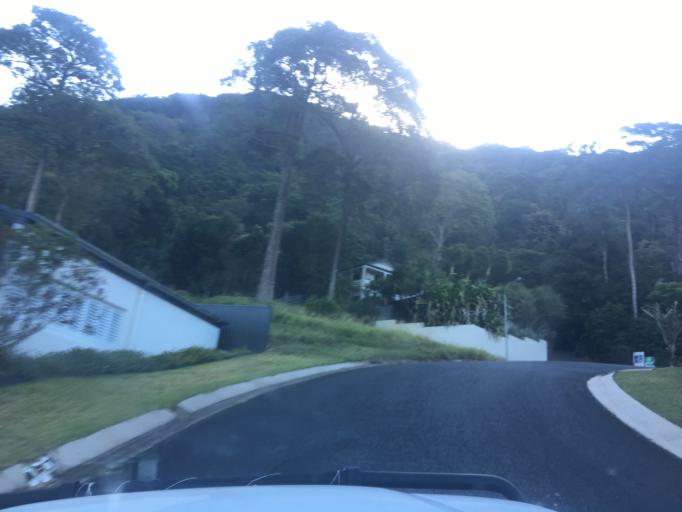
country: AU
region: Queensland
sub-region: Cairns
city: Woree
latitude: -16.9346
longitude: 145.7226
